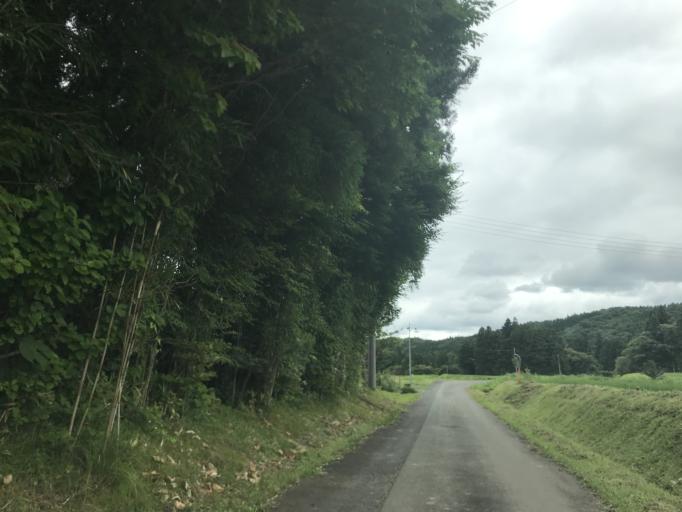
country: JP
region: Iwate
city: Ichinoseki
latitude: 38.9789
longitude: 140.9127
